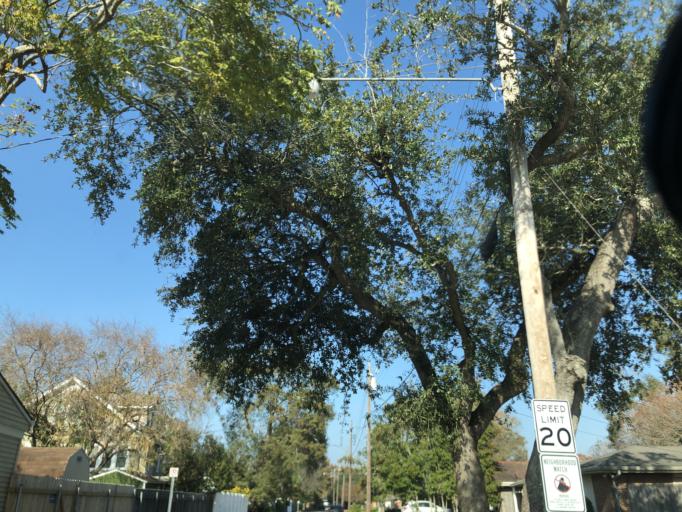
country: US
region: Louisiana
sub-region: Jefferson Parish
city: Metairie
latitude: 29.9893
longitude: -90.1504
